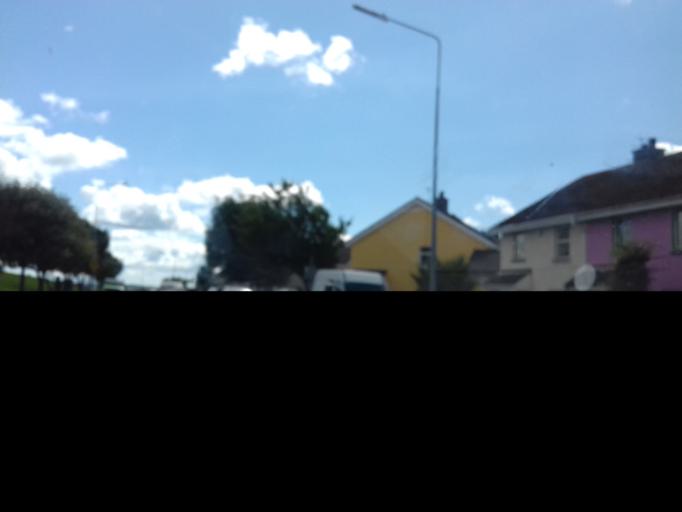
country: IE
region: Munster
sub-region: Waterford
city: Tra Mhor
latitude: 52.1675
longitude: -7.1415
